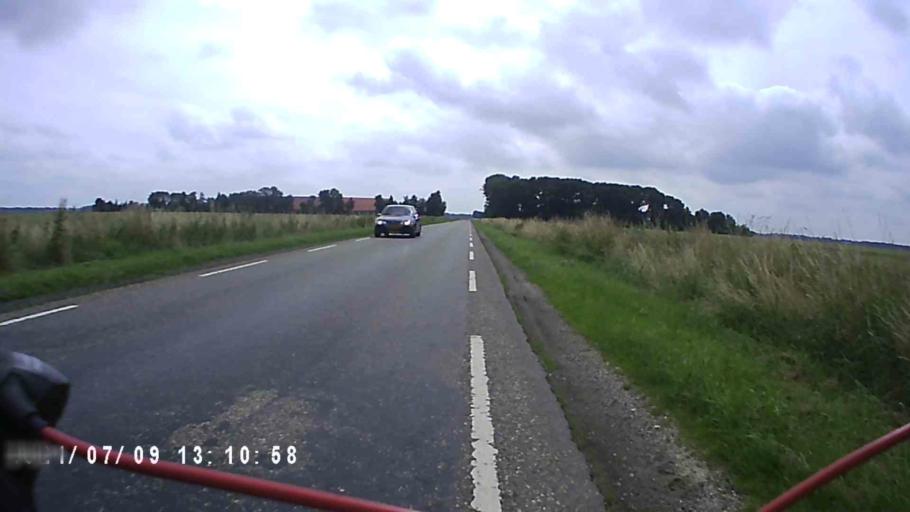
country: NL
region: Groningen
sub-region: Gemeente  Oldambt
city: Winschoten
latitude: 53.1268
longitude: 7.1275
